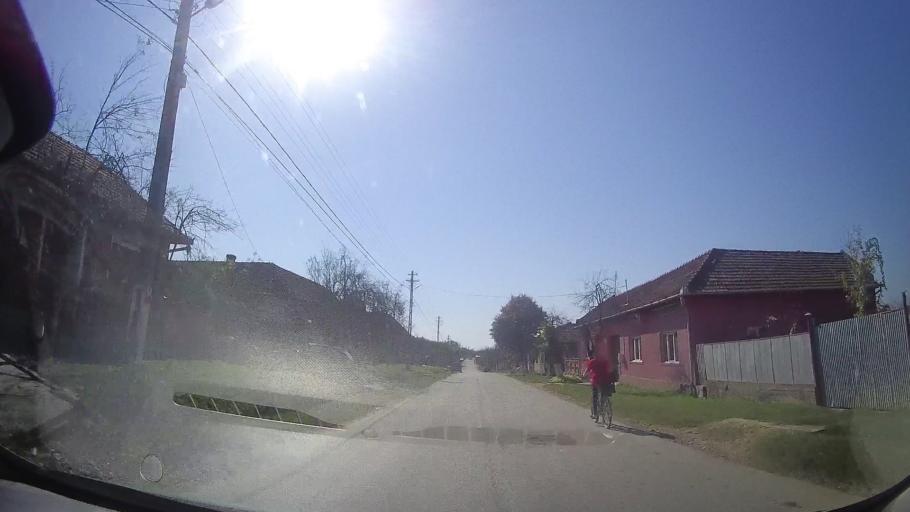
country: RO
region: Timis
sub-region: Comuna Bethausen
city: Bethausen
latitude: 45.8633
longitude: 21.9704
